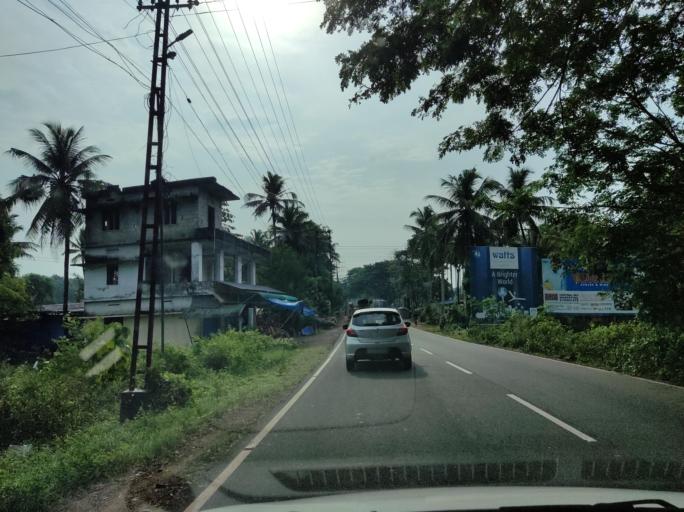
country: IN
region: Kerala
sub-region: Alappuzha
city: Kattanam
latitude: 9.1737
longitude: 76.5834
